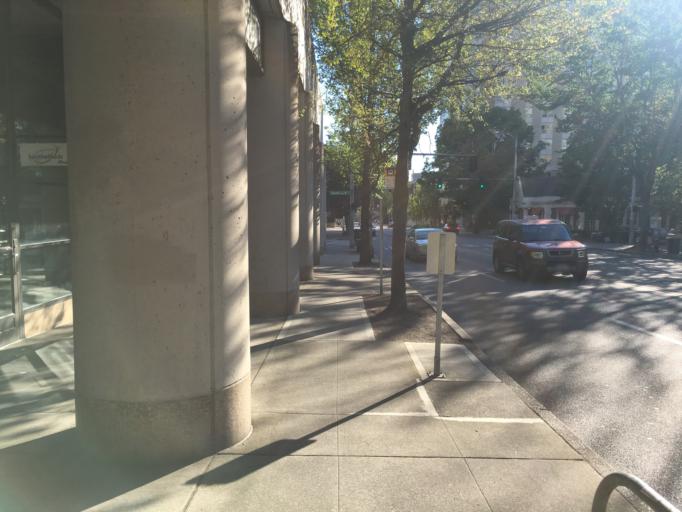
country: US
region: Washington
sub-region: King County
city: Seattle
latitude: 47.6105
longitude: -122.3223
